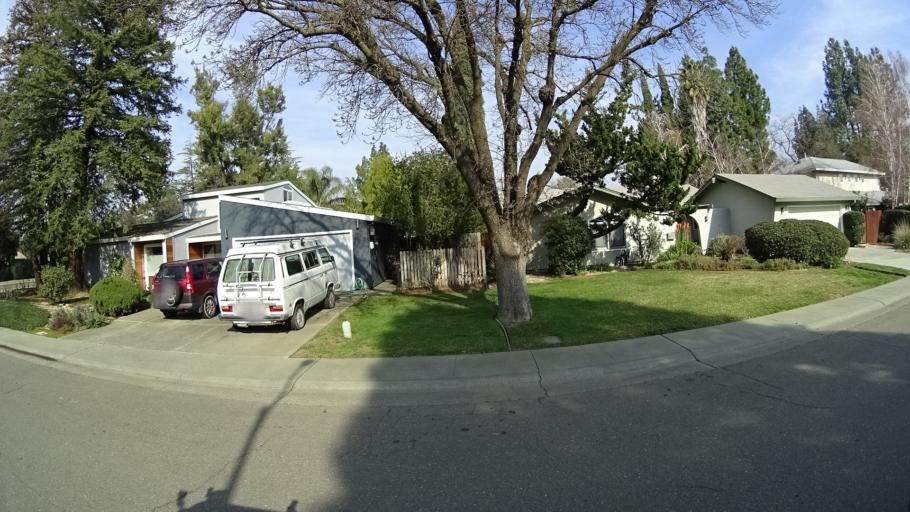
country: US
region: California
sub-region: Yolo County
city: Davis
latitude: 38.5650
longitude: -121.7580
